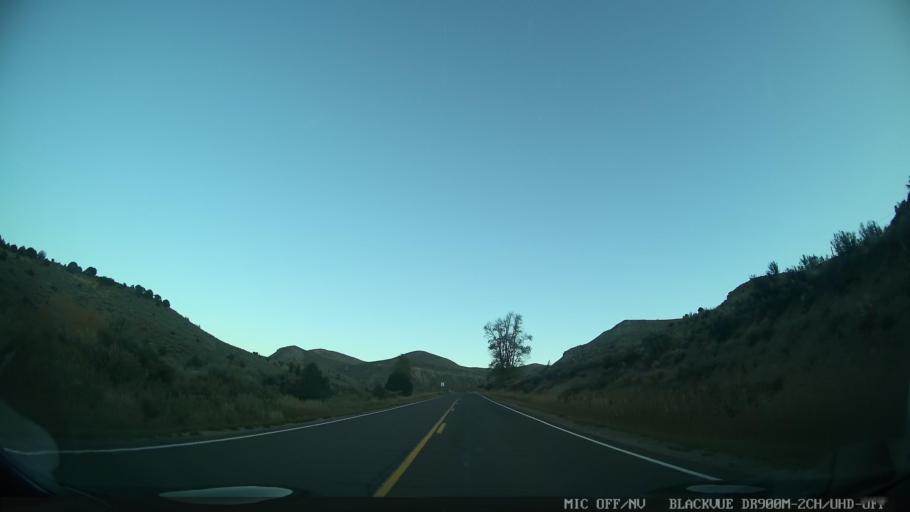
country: US
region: Colorado
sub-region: Eagle County
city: Edwards
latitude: 39.7650
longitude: -106.6781
